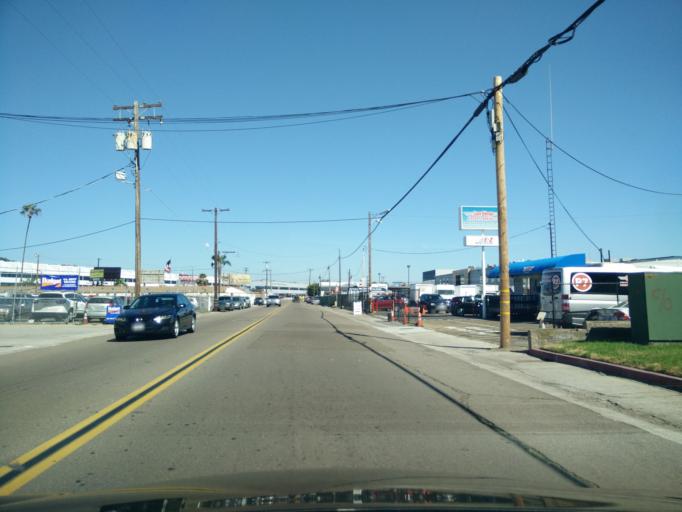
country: US
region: California
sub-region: San Diego County
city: San Diego
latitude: 32.7511
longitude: -117.2020
